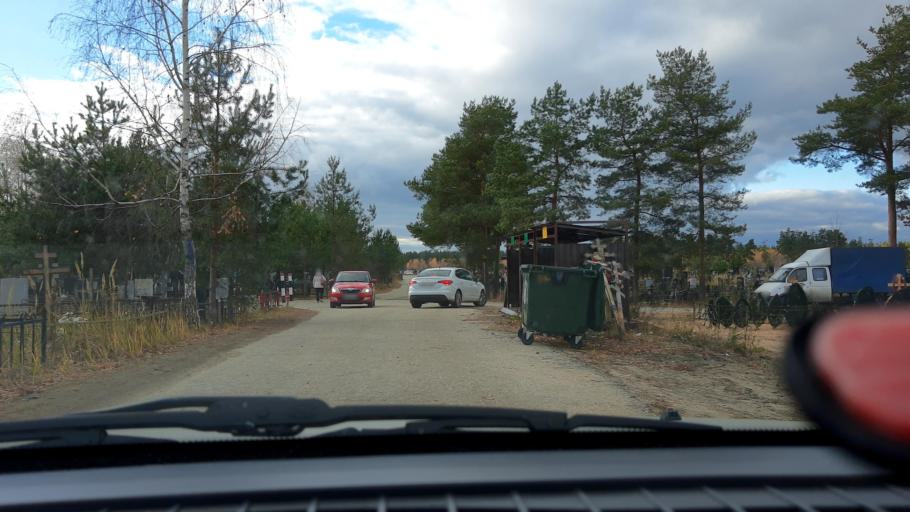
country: RU
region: Nizjnij Novgorod
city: Gorbatovka
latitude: 56.3602
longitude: 43.7712
